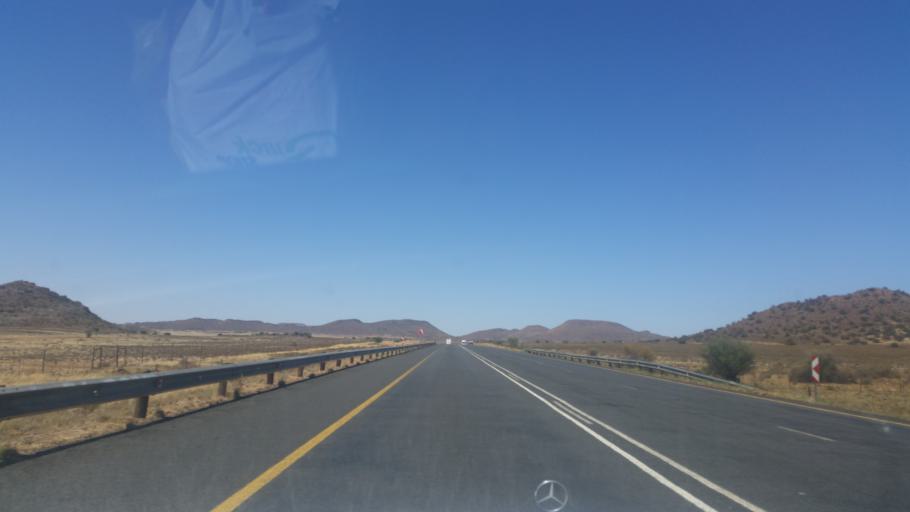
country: ZA
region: Northern Cape
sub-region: Pixley ka Seme District Municipality
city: Colesberg
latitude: -30.6200
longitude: 25.3364
